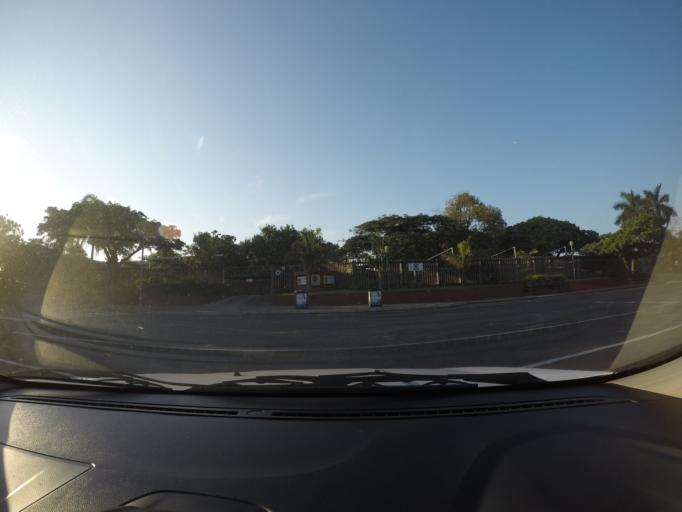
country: ZA
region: KwaZulu-Natal
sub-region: uThungulu District Municipality
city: Richards Bay
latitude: -28.7800
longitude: 32.0979
